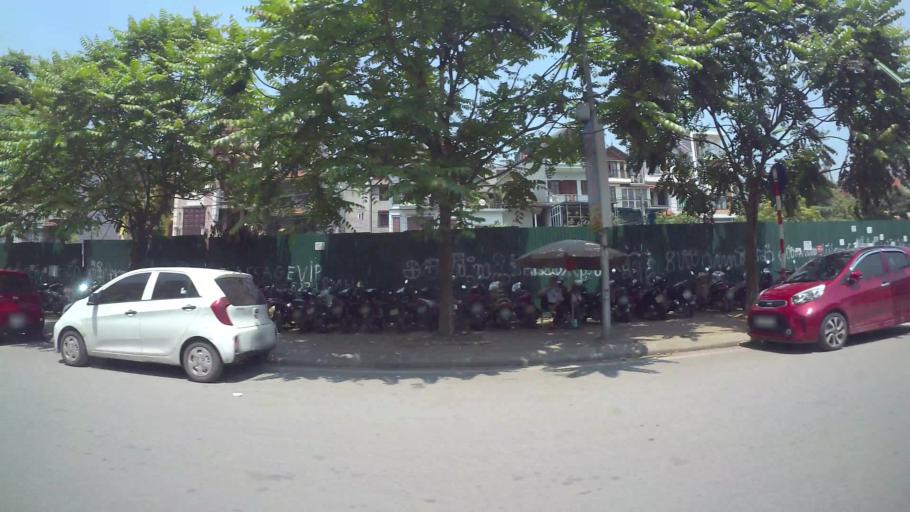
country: VN
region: Ha Noi
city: Hoan Kiem
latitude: 21.0413
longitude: 105.8766
